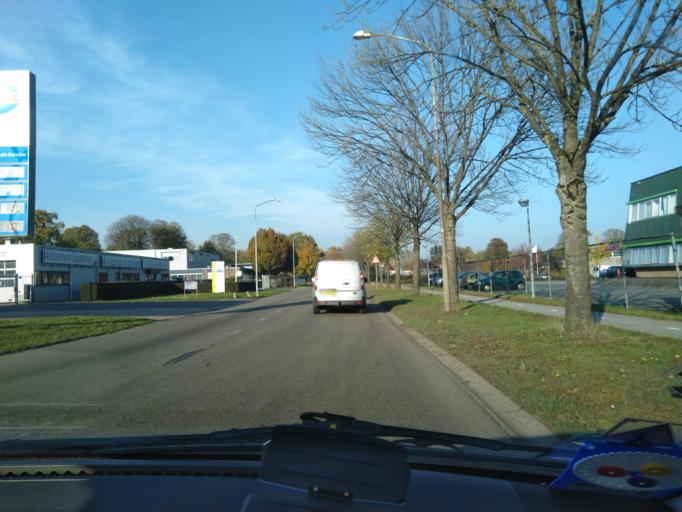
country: NL
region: Groningen
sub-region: Gemeente Hoogezand-Sappemeer
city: Sappemeer
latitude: 53.1626
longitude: 6.8103
